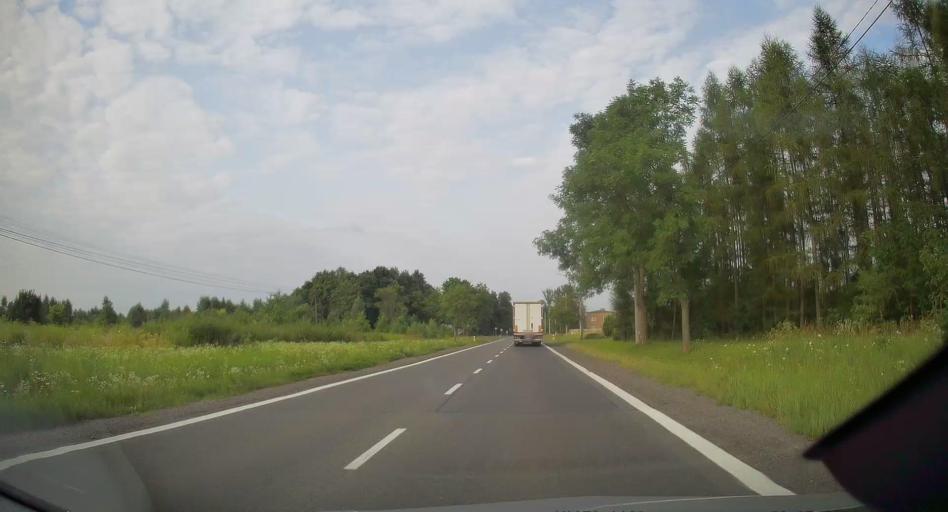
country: PL
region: Silesian Voivodeship
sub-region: Powiat czestochowski
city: Rudniki
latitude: 50.8875
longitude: 19.2626
